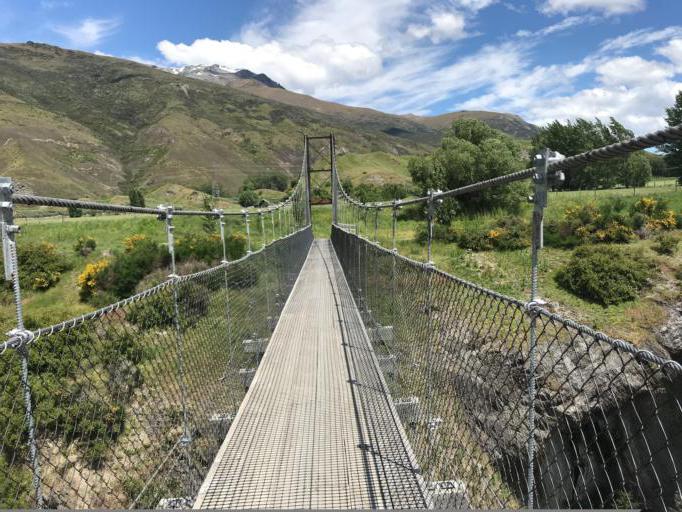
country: NZ
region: Otago
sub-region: Queenstown-Lakes District
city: Arrowtown
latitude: -45.0013
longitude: 168.8737
